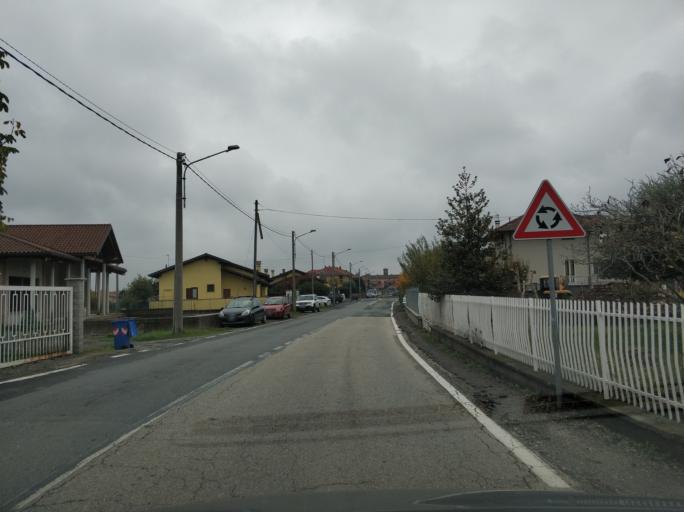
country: IT
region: Piedmont
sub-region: Provincia di Torino
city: Villanova Canavese
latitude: 45.2464
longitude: 7.5562
